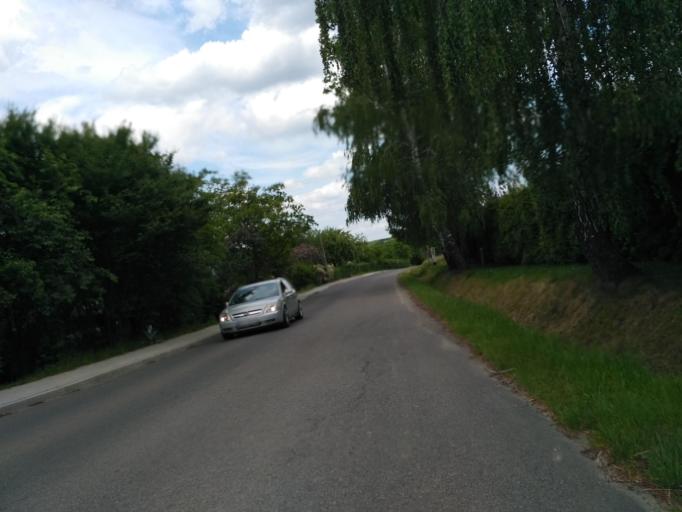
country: PL
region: Subcarpathian Voivodeship
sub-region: Powiat krosnienski
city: Chorkowka
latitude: 49.6446
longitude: 21.6686
